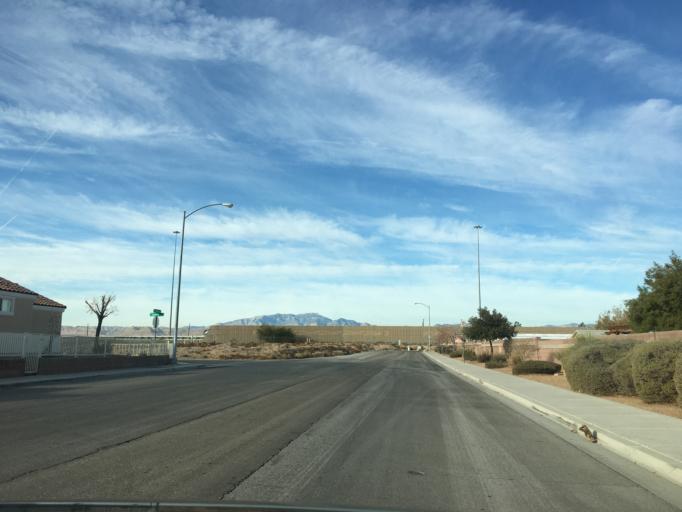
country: US
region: Nevada
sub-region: Clark County
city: Enterprise
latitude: 36.0173
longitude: -115.1783
